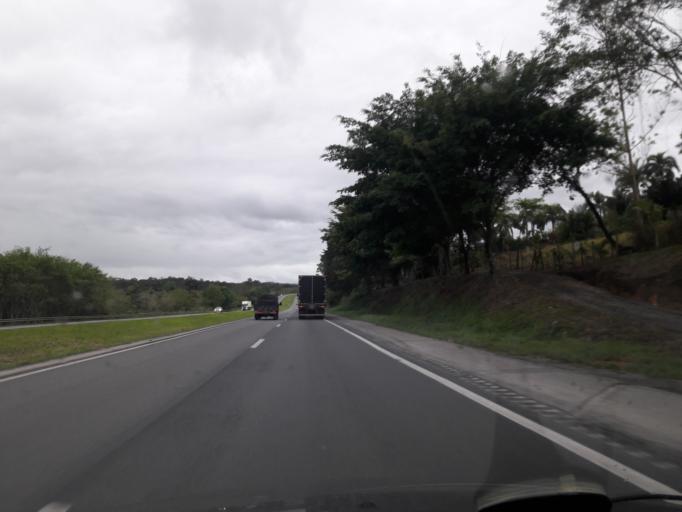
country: BR
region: Sao Paulo
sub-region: Miracatu
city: Miracatu
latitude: -24.2840
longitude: -47.4363
